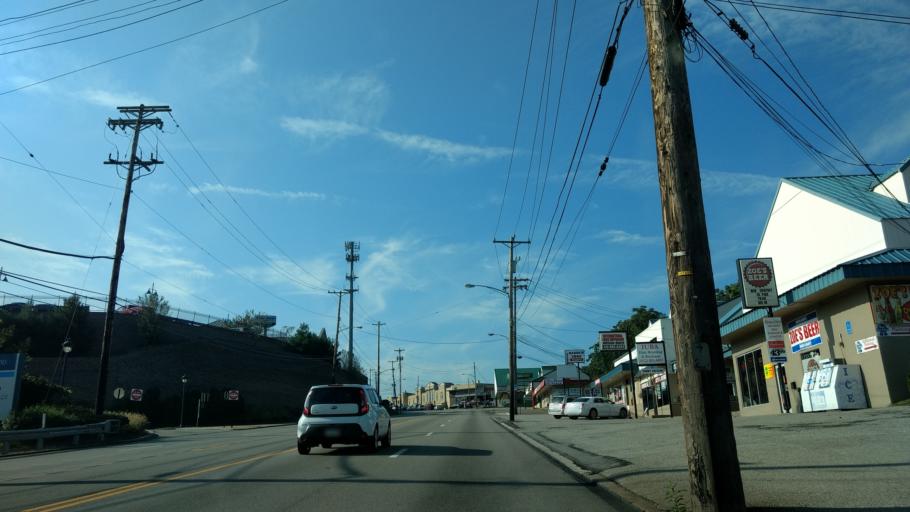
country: US
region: Pennsylvania
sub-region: Allegheny County
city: Whitehall
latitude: 40.3674
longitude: -79.9841
